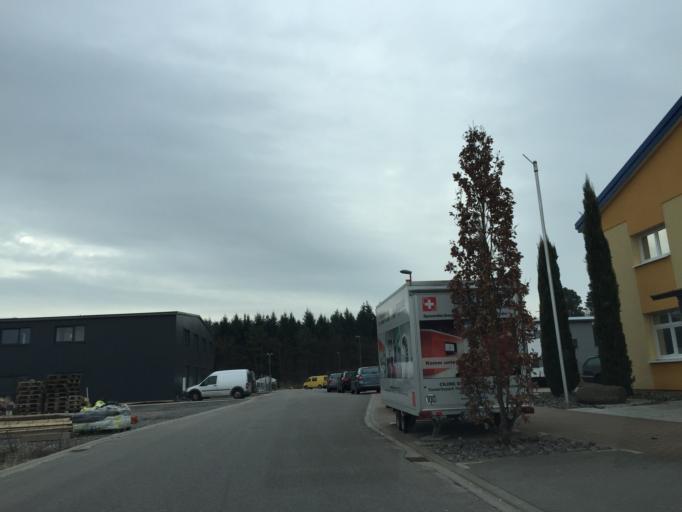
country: DE
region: Baden-Wuerttemberg
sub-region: Karlsruhe Region
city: Oftersheim
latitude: 49.3540
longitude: 8.5856
